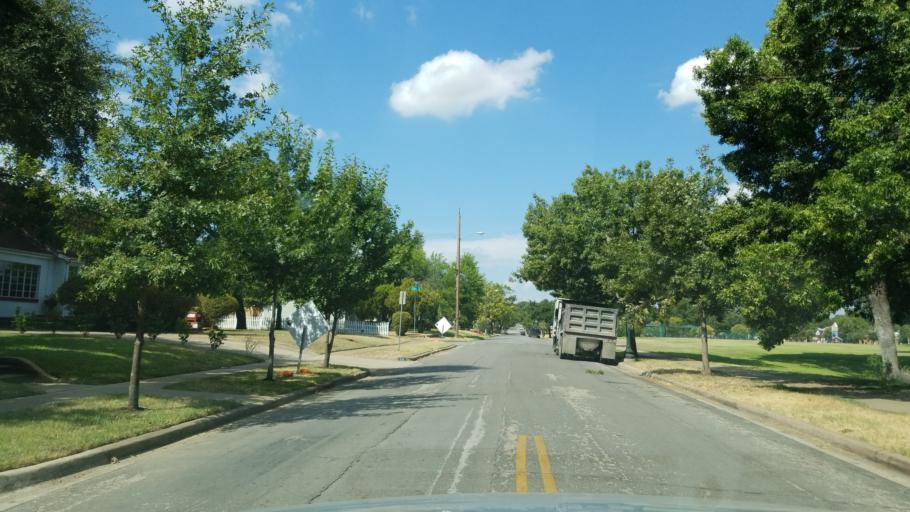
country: US
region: Texas
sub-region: Dallas County
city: Dallas
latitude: 32.7548
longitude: -96.8169
